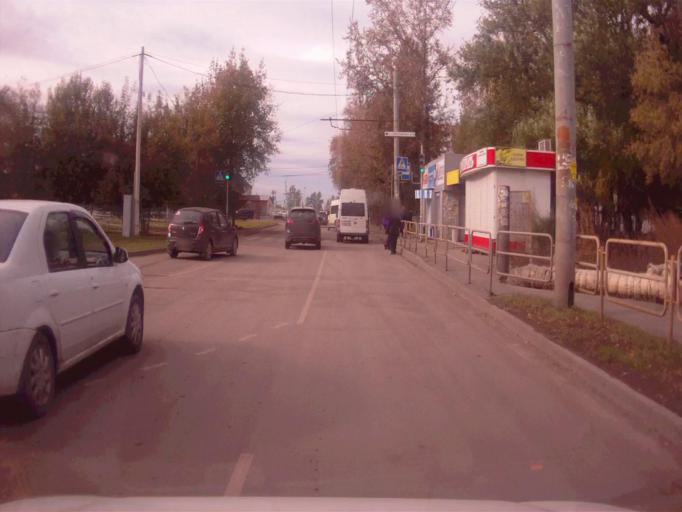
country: RU
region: Chelyabinsk
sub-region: Gorod Chelyabinsk
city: Chelyabinsk
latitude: 55.1161
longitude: 61.4260
